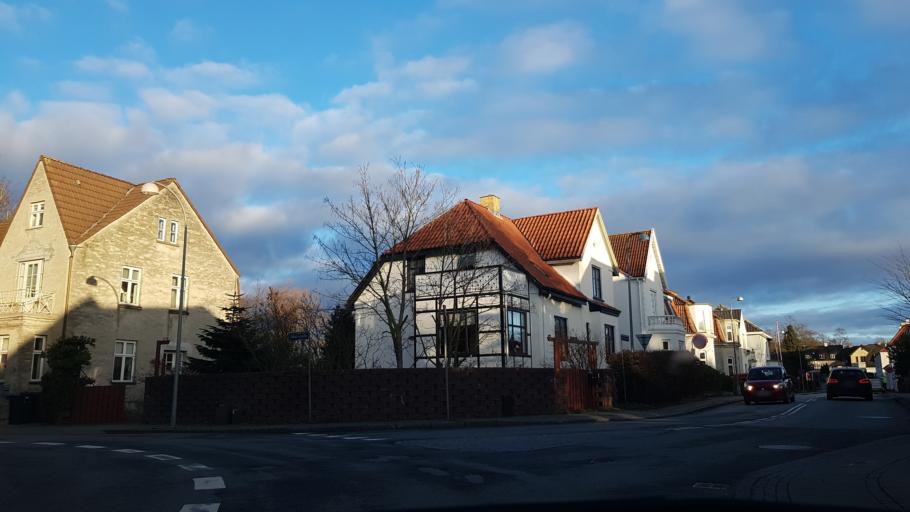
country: DK
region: Zealand
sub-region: Slagelse Kommune
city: Slagelse
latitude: 55.4035
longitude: 11.3580
